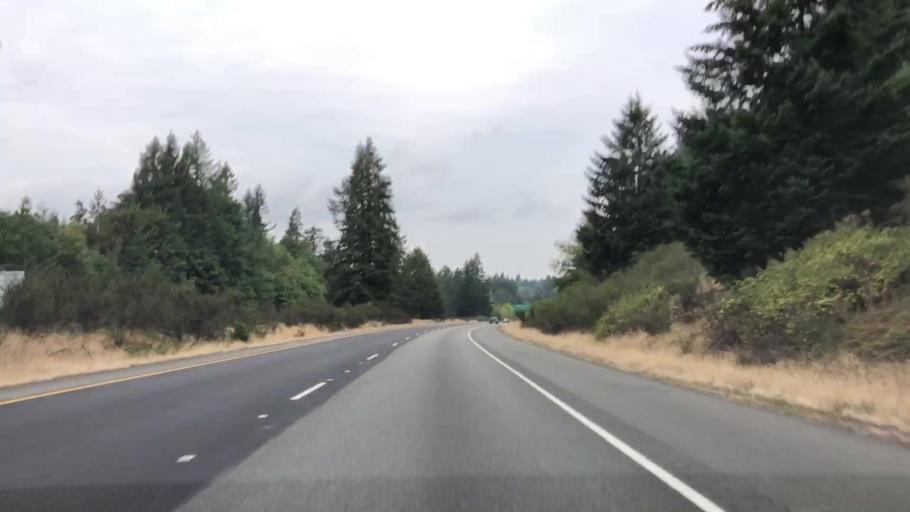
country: US
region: Washington
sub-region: Kitsap County
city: Port Orchard
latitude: 47.5159
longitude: -122.6566
